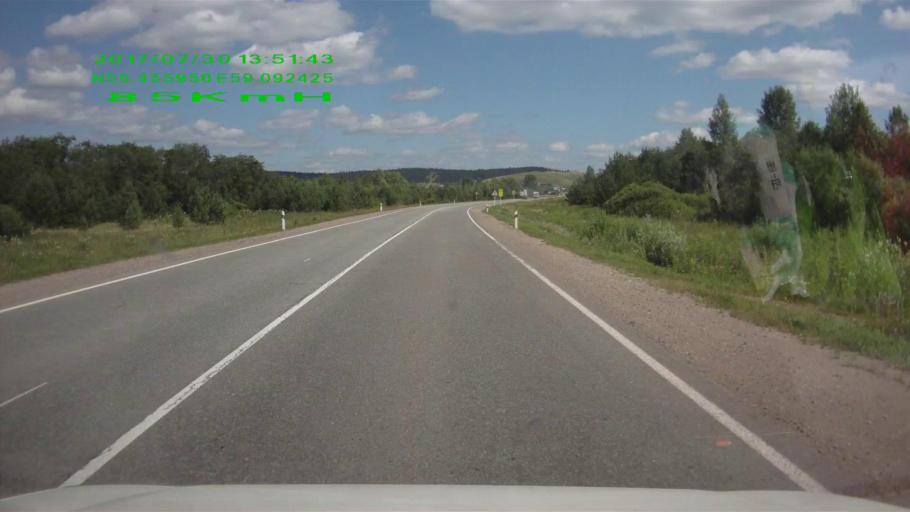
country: RU
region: Sverdlovsk
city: Mikhaylovsk
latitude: 56.4561
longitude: 59.0930
